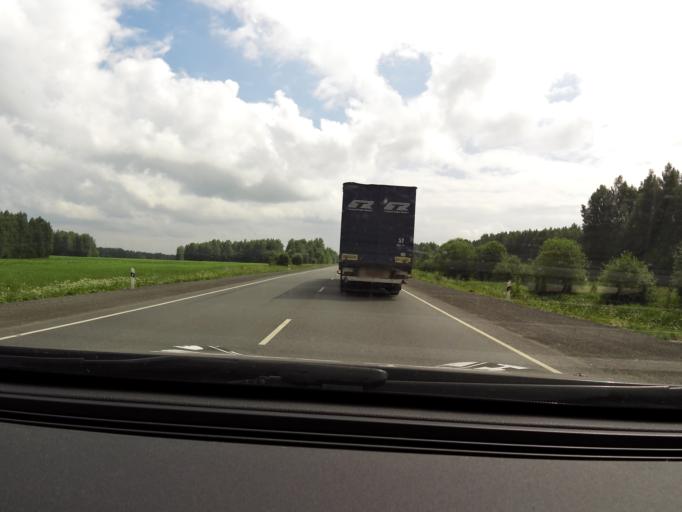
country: RU
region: Perm
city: Ust'-Kishert'
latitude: 57.1702
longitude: 57.1460
